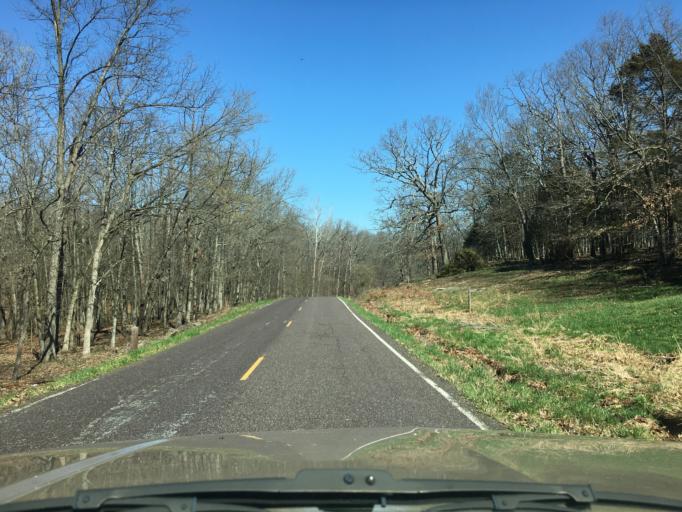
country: US
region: Missouri
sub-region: Franklin County
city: New Haven
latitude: 38.5411
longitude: -91.3297
